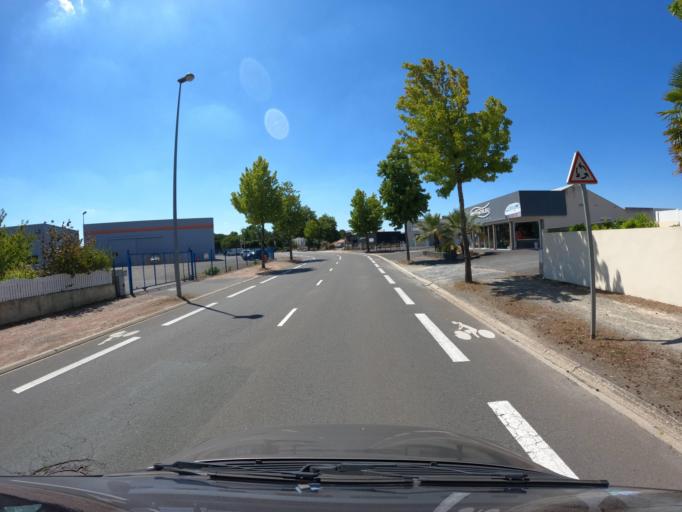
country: FR
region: Pays de la Loire
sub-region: Departement de la Vendee
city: Challans
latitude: 46.8422
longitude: -1.8619
